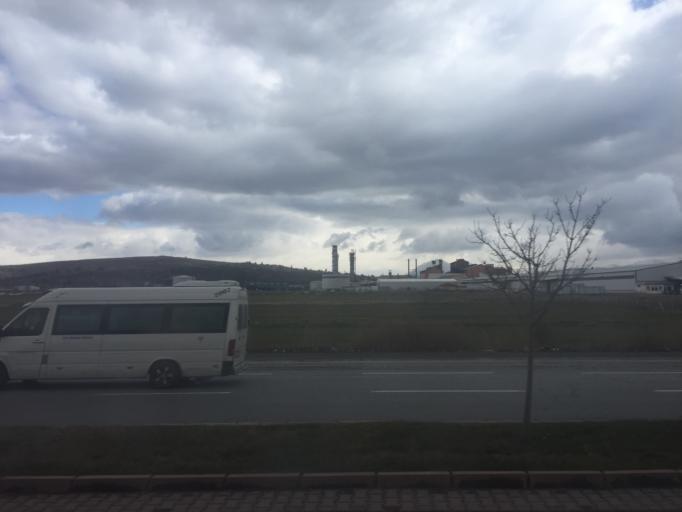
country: TR
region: Kayseri
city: Melikgazi
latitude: 38.7534
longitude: 35.4074
